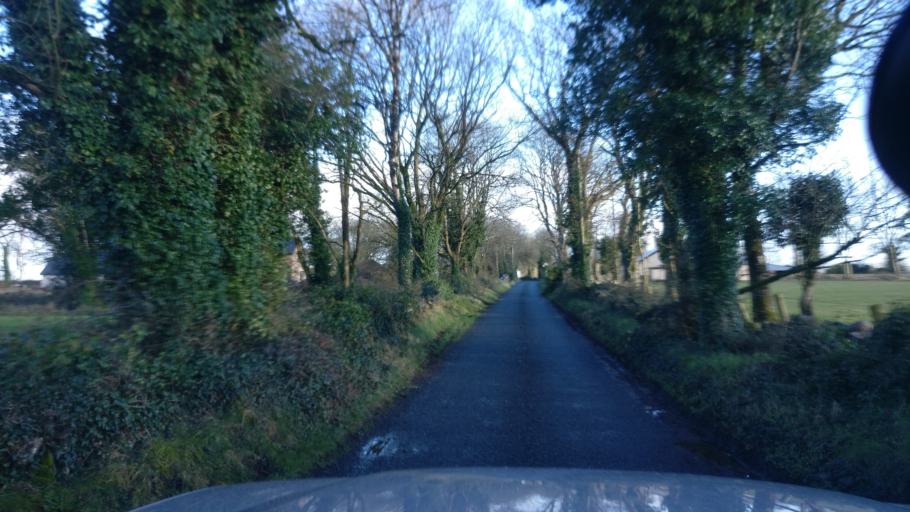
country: IE
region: Connaught
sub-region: County Galway
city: Loughrea
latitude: 53.2300
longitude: -8.5769
